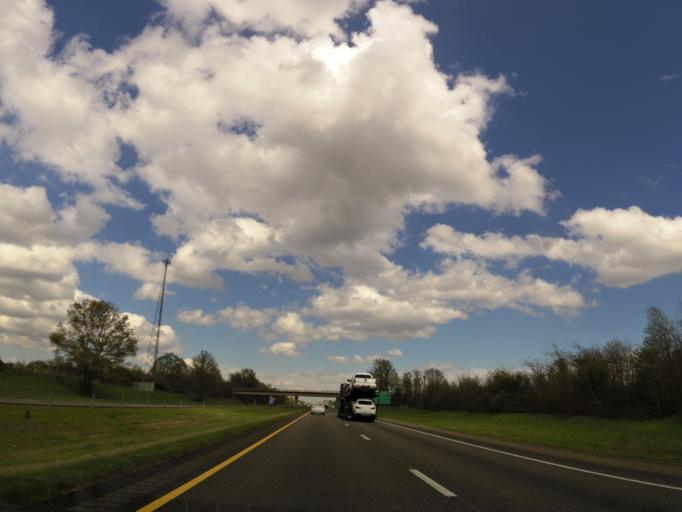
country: US
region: Tennessee
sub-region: Madison County
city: Jackson
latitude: 35.6379
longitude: -88.9323
